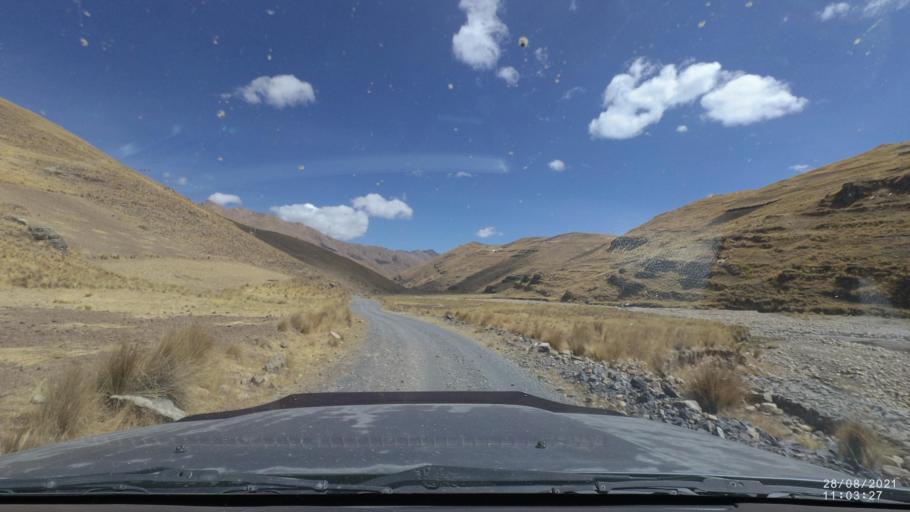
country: BO
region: Cochabamba
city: Cochabamba
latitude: -17.1763
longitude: -66.2767
